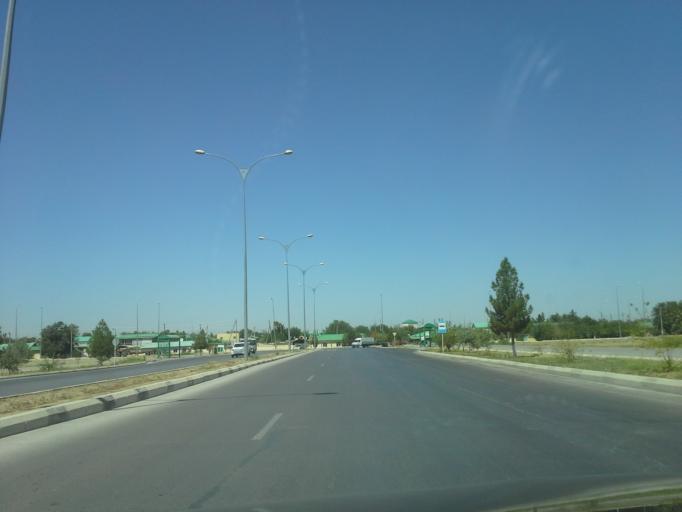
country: TM
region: Ahal
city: Ashgabat
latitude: 38.0068
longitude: 58.3080
